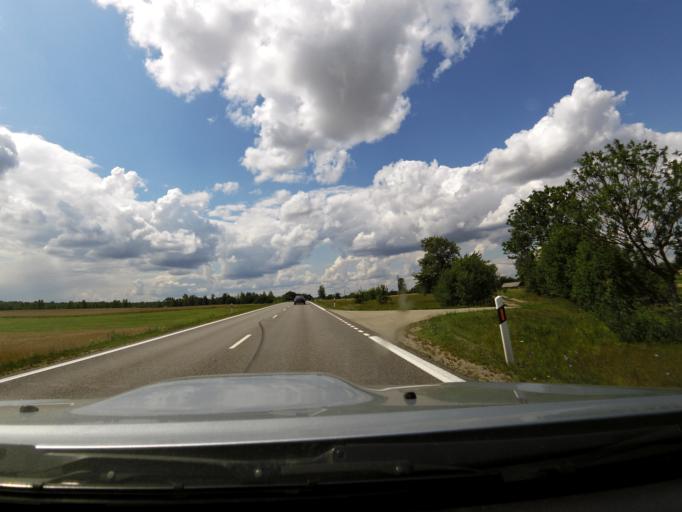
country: LT
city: Jieznas
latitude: 54.5797
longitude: 24.2951
